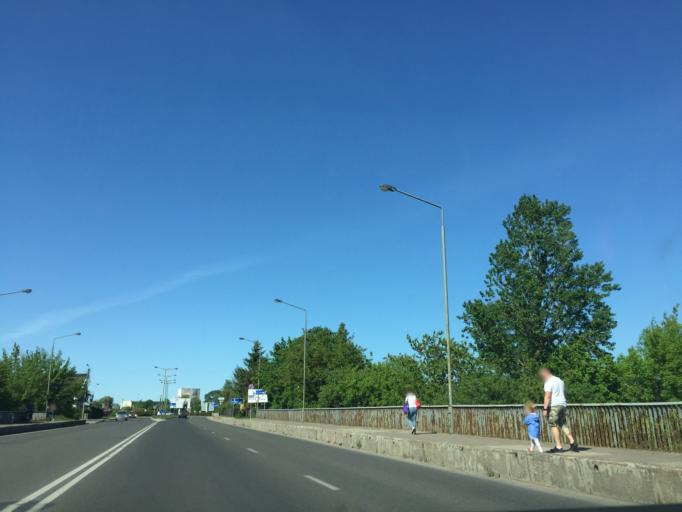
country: LT
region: Panevezys
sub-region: Panevezys City
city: Panevezys
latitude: 55.7413
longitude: 24.3397
